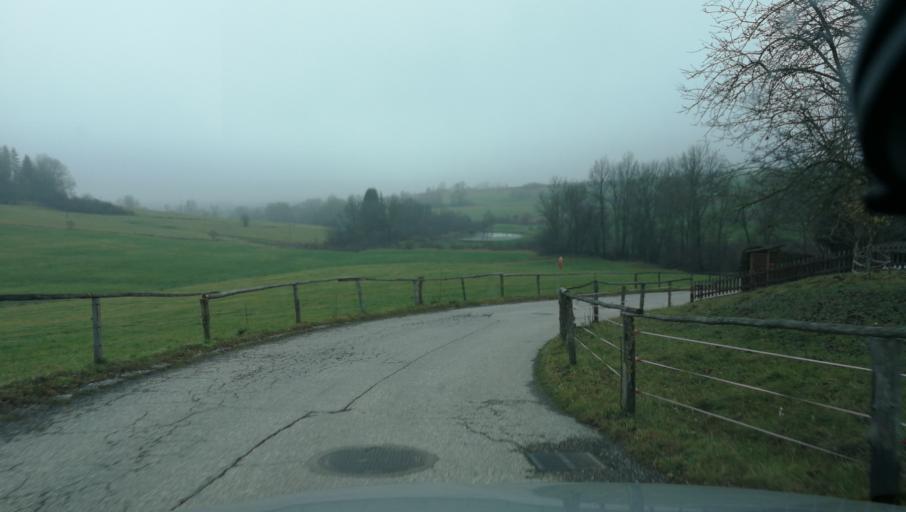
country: AT
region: Styria
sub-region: Politischer Bezirk Leoben
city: Trofaiach
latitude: 47.4253
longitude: 14.9677
